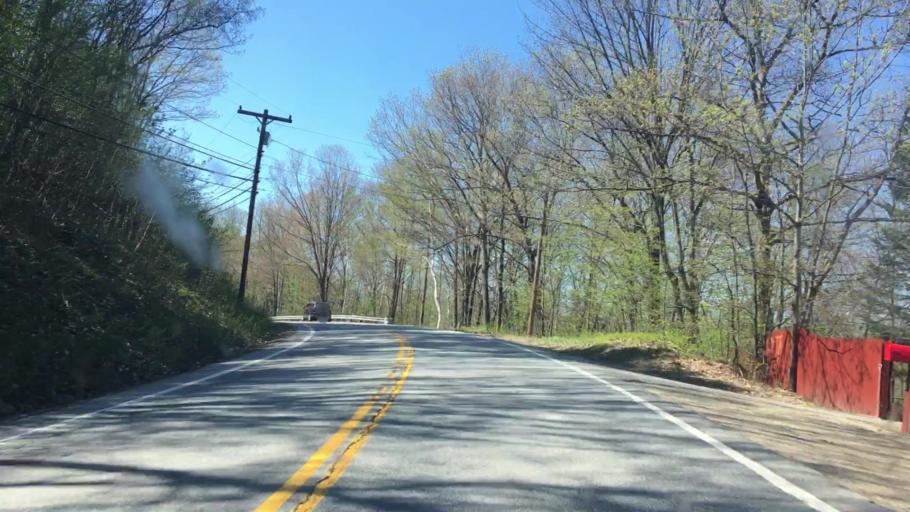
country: US
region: New Hampshire
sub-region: Grafton County
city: Plymouth
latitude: 43.7457
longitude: -71.6807
